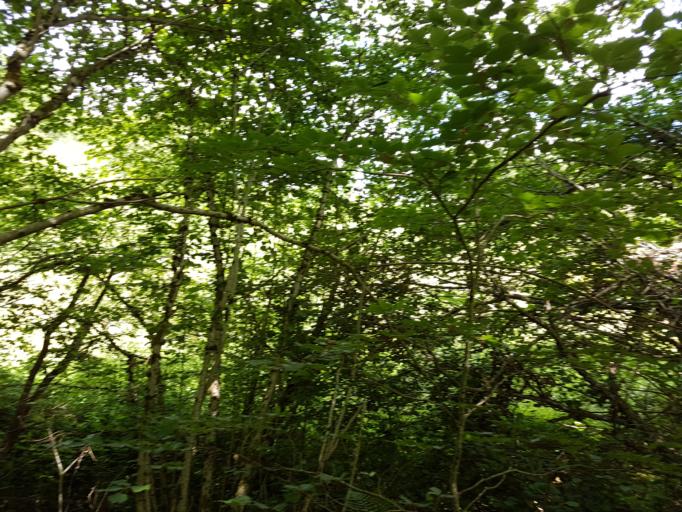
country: FR
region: Bourgogne
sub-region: Departement de la Cote-d'Or
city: Saulieu
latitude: 47.1820
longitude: 4.0842
